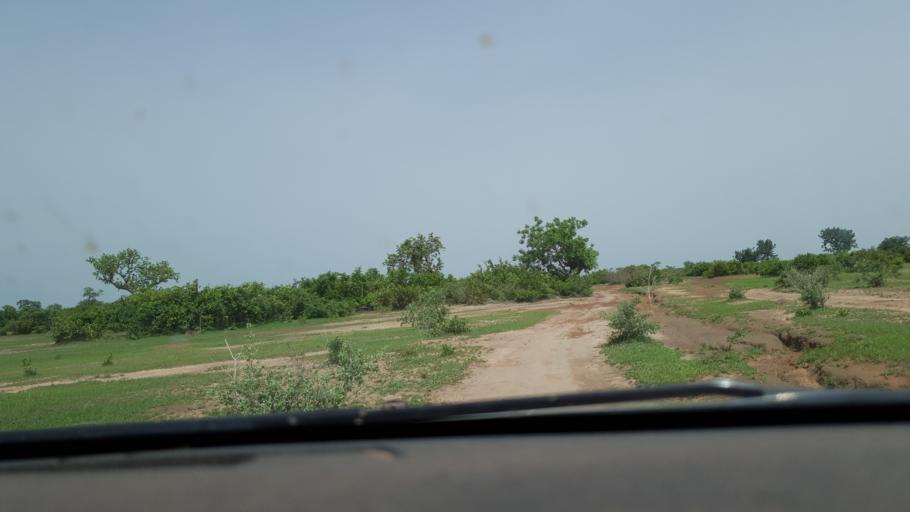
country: ML
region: Koulikoro
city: Koulikoro
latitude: 12.6653
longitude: -7.2256
